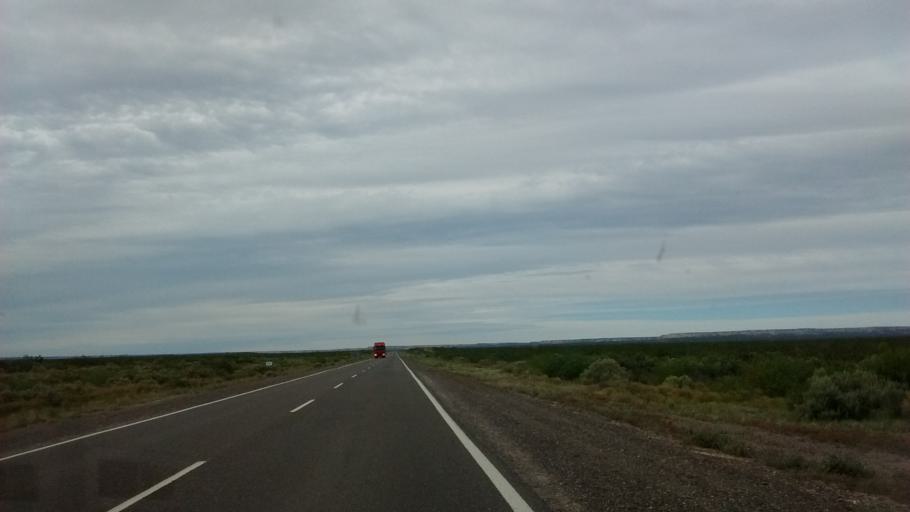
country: AR
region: Rio Negro
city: Catriel
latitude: -38.0787
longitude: -67.9244
